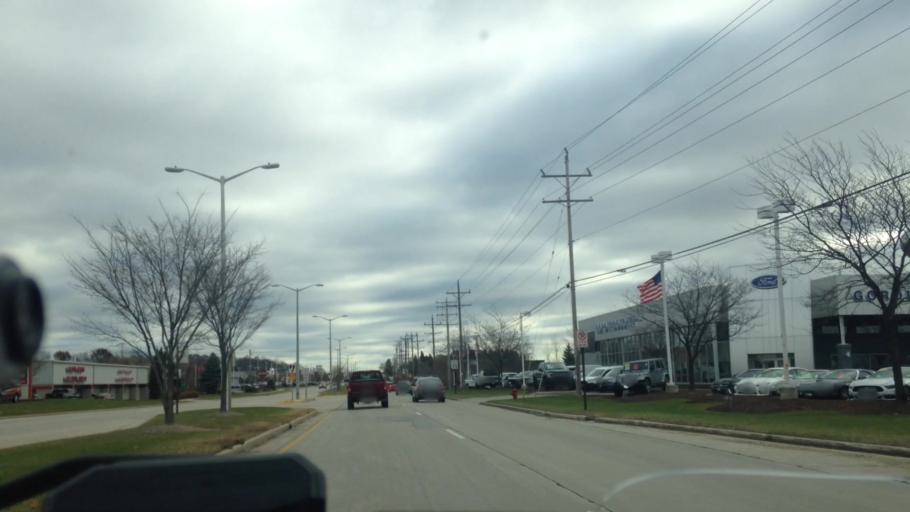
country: US
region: Wisconsin
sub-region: Washington County
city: West Bend
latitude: 43.4272
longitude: -88.2258
